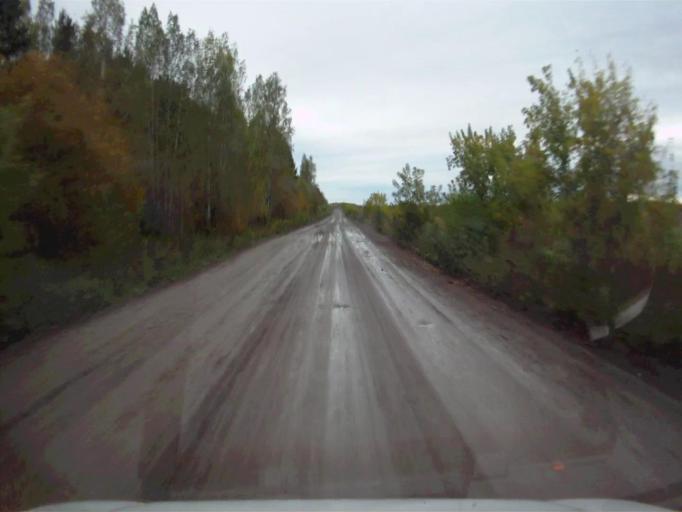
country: RU
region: Sverdlovsk
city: Mikhaylovsk
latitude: 56.1589
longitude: 59.2524
